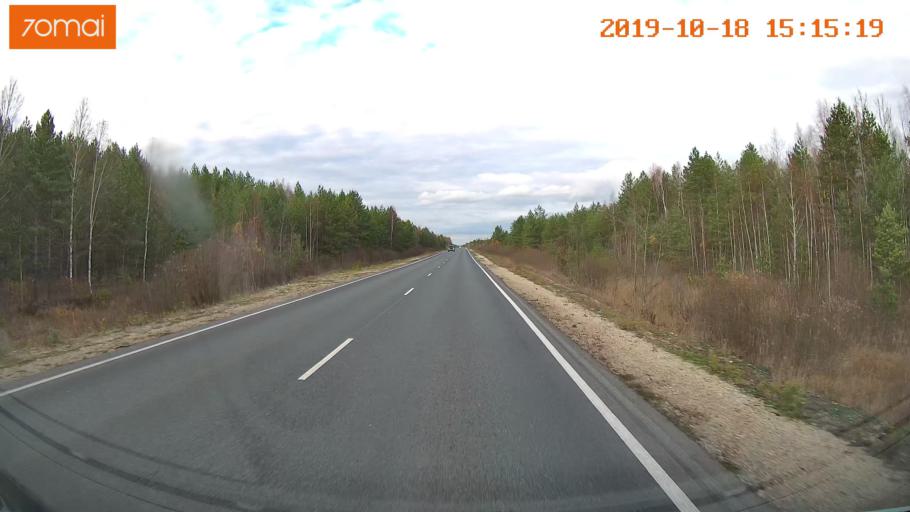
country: RU
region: Vladimir
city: Gus'-Khrustal'nyy
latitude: 55.6170
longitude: 40.7222
